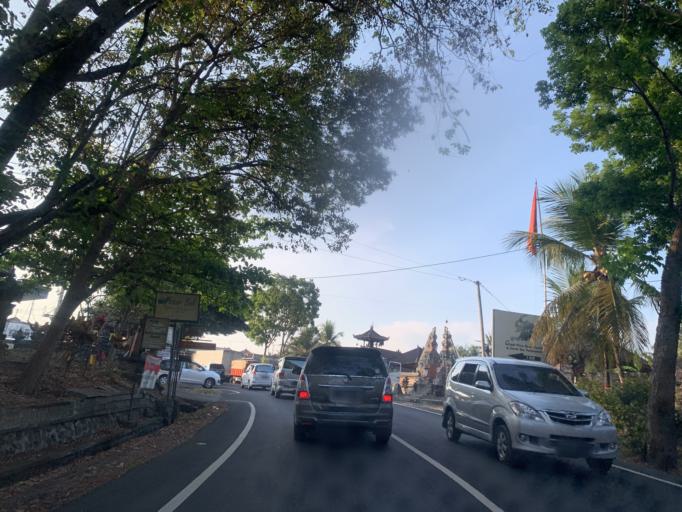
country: ID
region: Bali
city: Banjar Delodrurung
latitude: -8.4955
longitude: 114.9662
